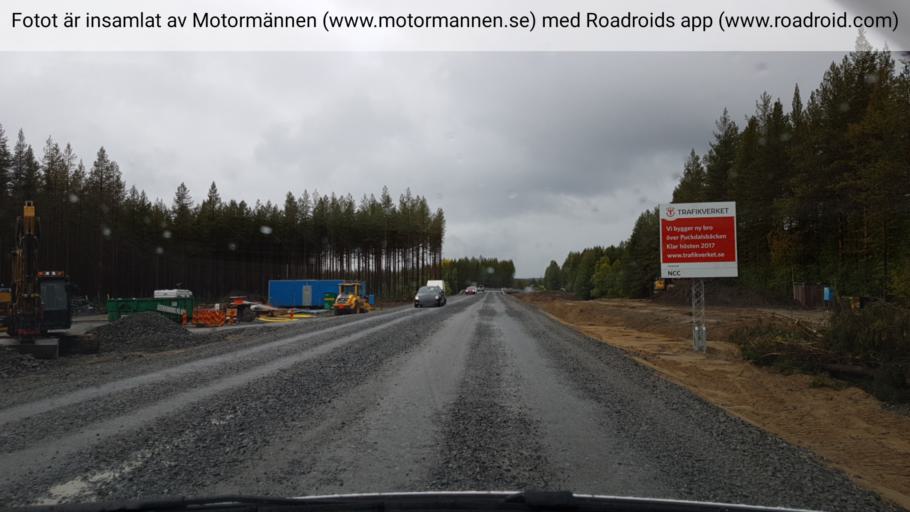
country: SE
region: Vaesterbotten
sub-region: Vindelns Kommun
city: Vindeln
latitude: 64.1743
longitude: 19.7409
